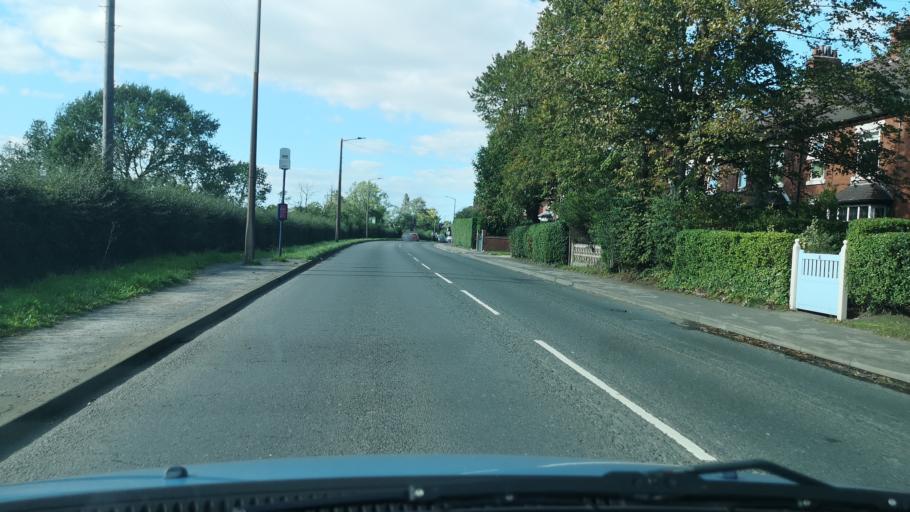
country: GB
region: England
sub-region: Doncaster
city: Kirk Sandall
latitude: 53.5708
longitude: -1.0661
